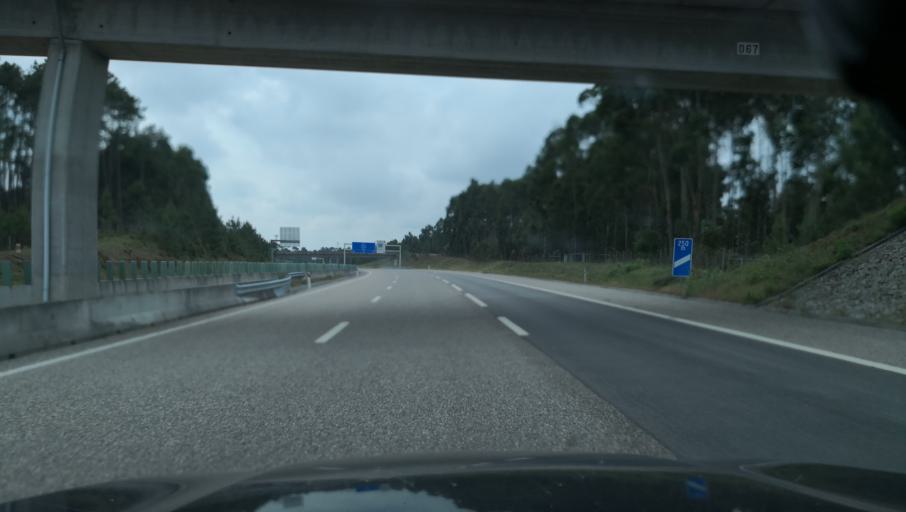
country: PT
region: Leiria
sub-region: Pombal
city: Lourical
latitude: 39.9960
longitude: -8.7983
